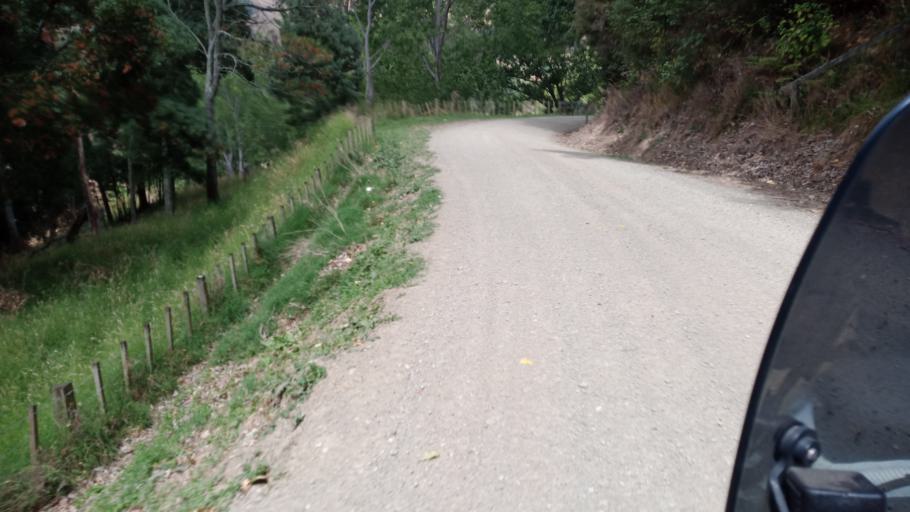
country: NZ
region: Gisborne
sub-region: Gisborne District
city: Gisborne
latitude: -38.4822
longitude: 177.6900
